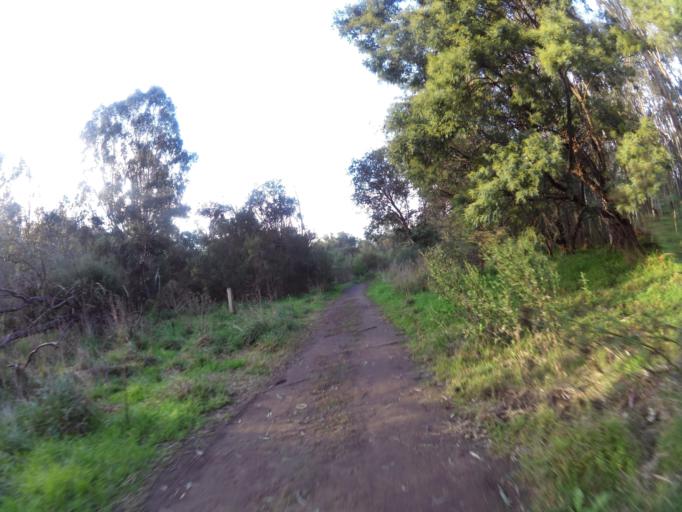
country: AU
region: Victoria
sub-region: Banyule
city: Viewbank
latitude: -37.7520
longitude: 145.0910
